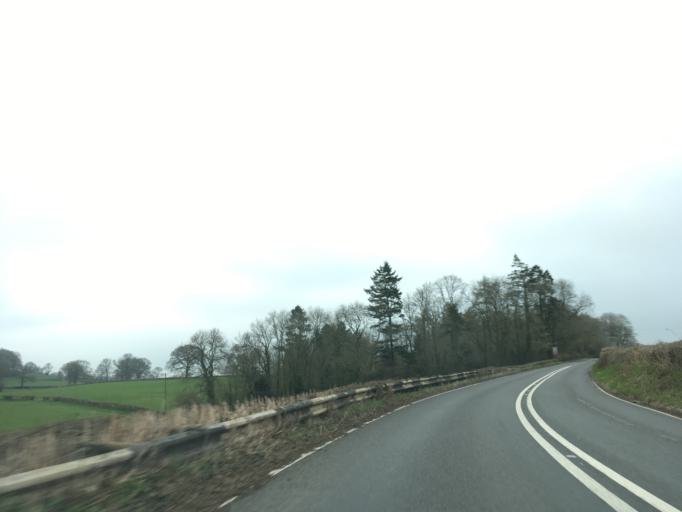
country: GB
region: Wales
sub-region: Monmouthshire
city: Llangybi
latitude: 51.6479
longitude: -2.9274
